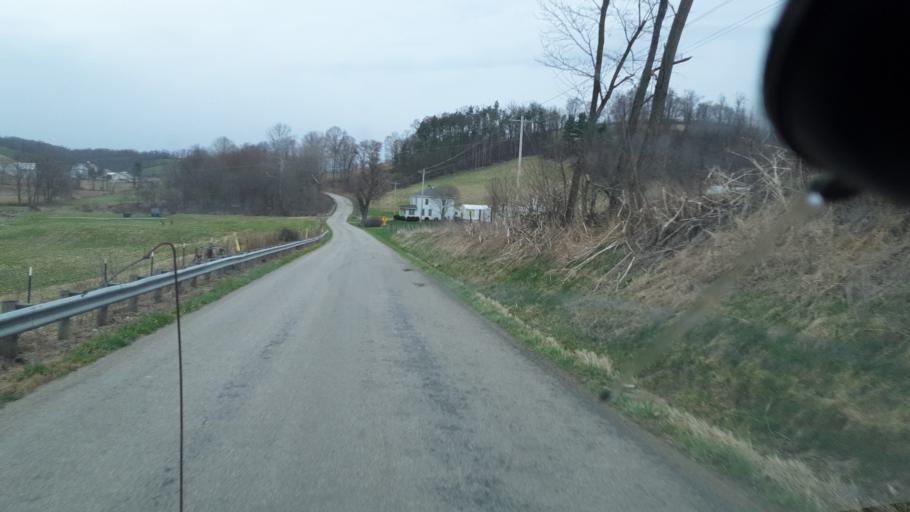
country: US
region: Ohio
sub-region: Coshocton County
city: West Lafayette
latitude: 40.3257
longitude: -81.6905
